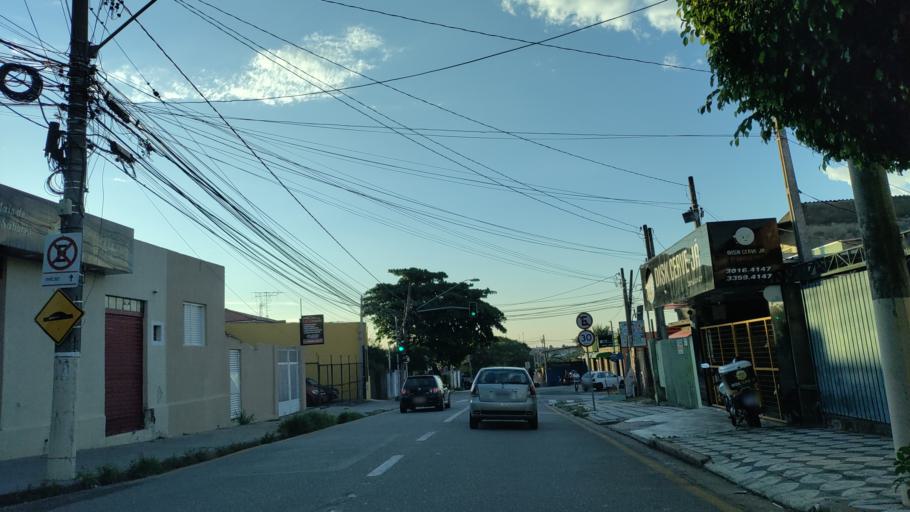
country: BR
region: Sao Paulo
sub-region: Sorocaba
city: Sorocaba
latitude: -23.4848
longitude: -47.4531
